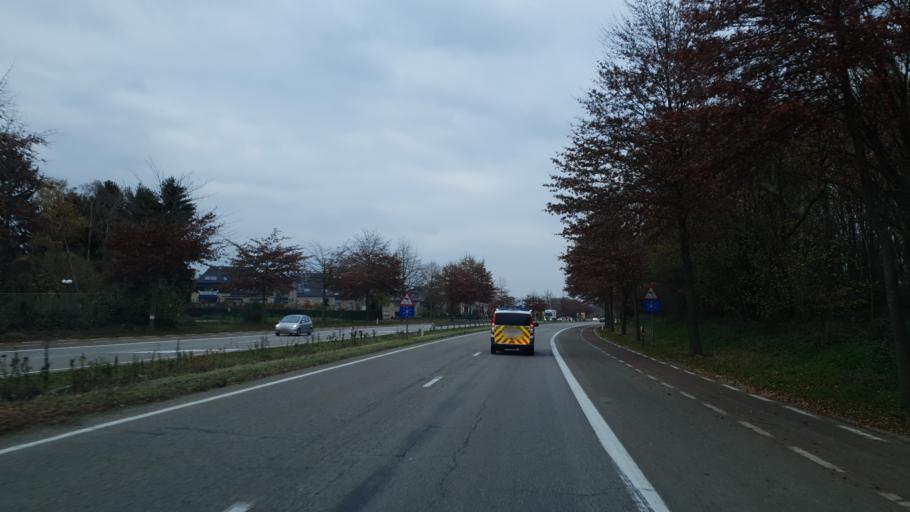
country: BE
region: Flanders
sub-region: Provincie Limburg
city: Lanaken
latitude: 50.8858
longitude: 5.6462
